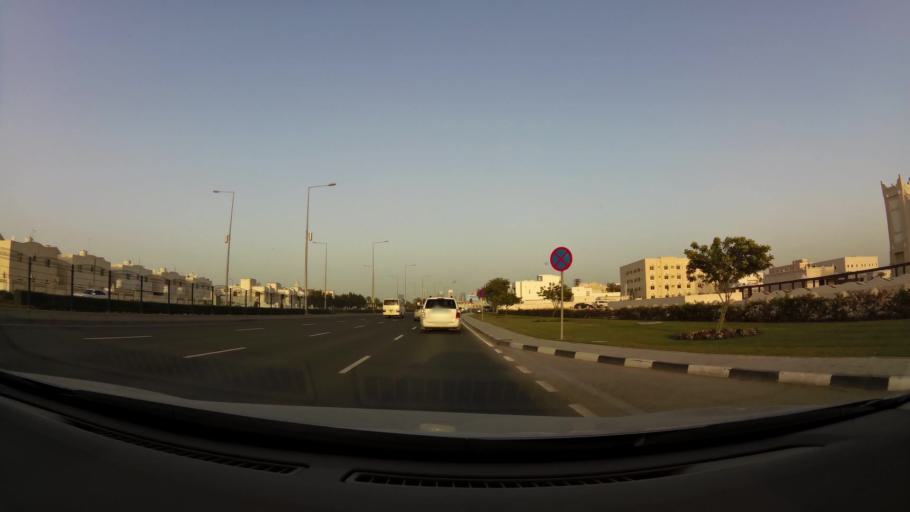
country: QA
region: Baladiyat ad Dawhah
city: Doha
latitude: 25.3227
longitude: 51.4795
